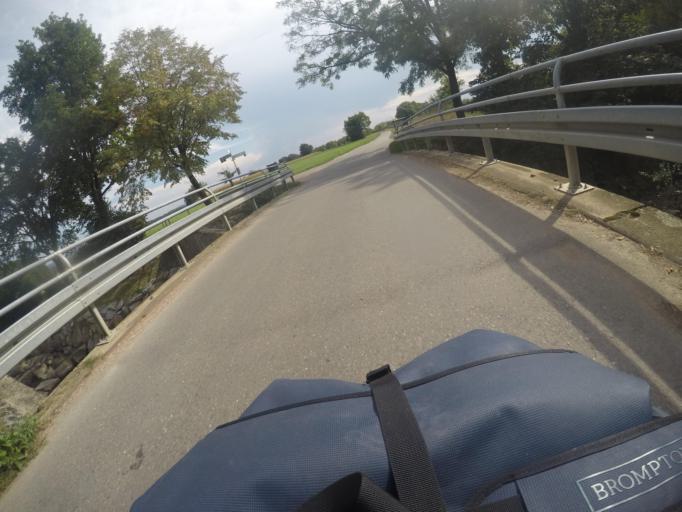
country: DE
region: Baden-Wuerttemberg
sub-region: Freiburg Region
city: Efringen-Kirchen
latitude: 47.6335
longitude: 7.5739
